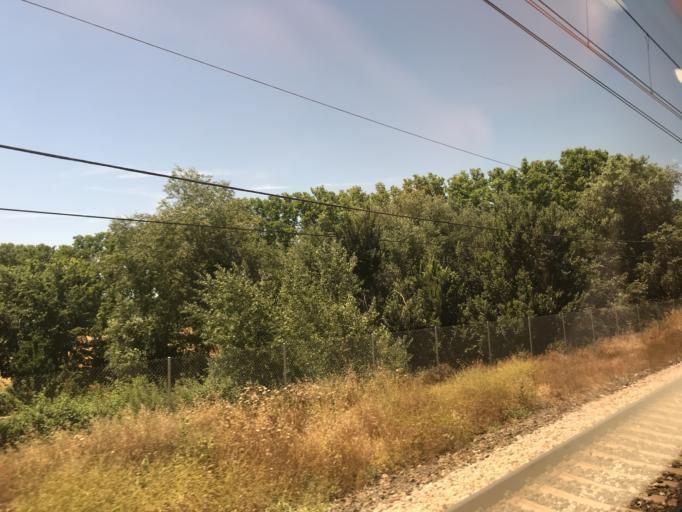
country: ES
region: Madrid
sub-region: Provincia de Madrid
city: Aranjuez
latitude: 40.0411
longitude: -3.6208
